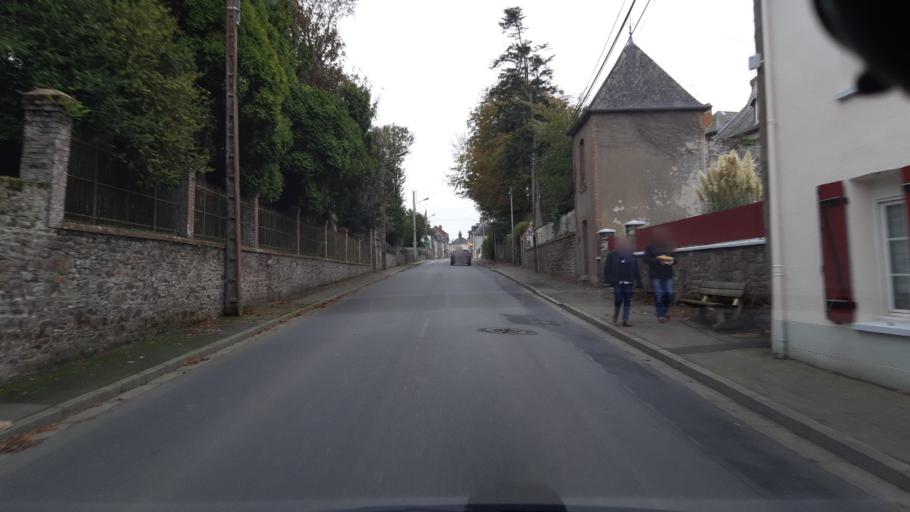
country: FR
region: Lower Normandy
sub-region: Departement de la Manche
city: Quettreville-sur-Sienne
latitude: 48.9187
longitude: -1.4314
